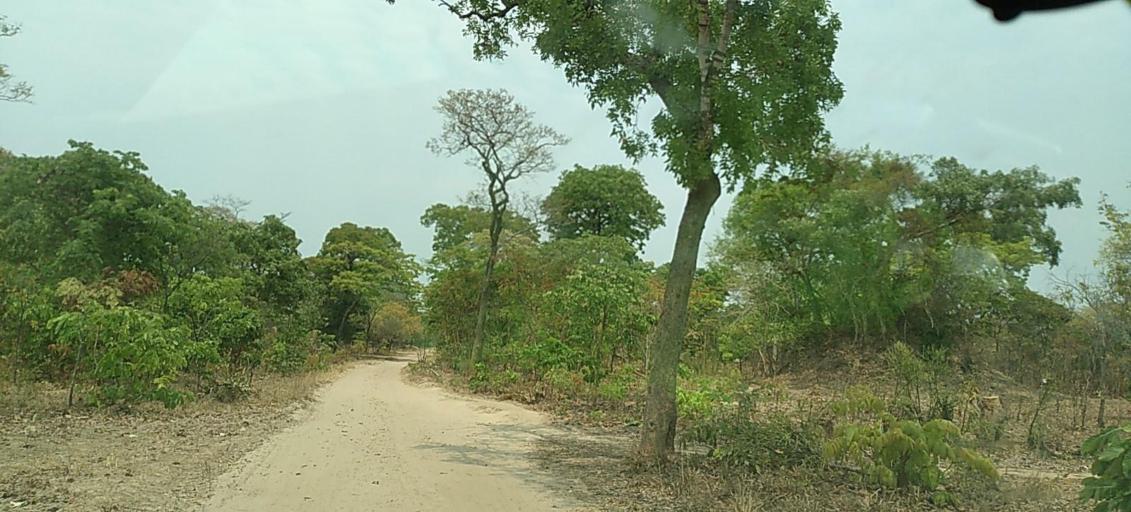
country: ZM
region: North-Western
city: Kabompo
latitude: -13.5560
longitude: 24.4475
